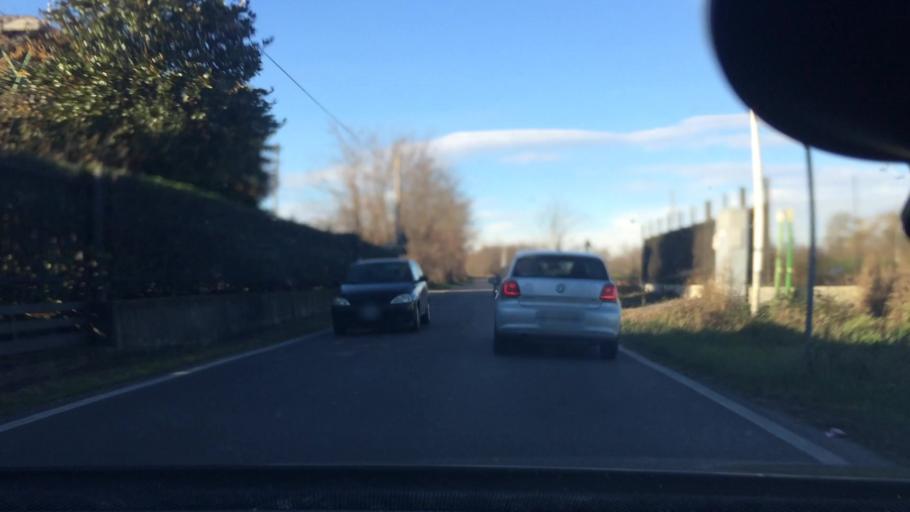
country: IT
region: Lombardy
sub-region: Citta metropolitana di Milano
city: Cerro Maggiore
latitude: 45.6013
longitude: 8.9535
